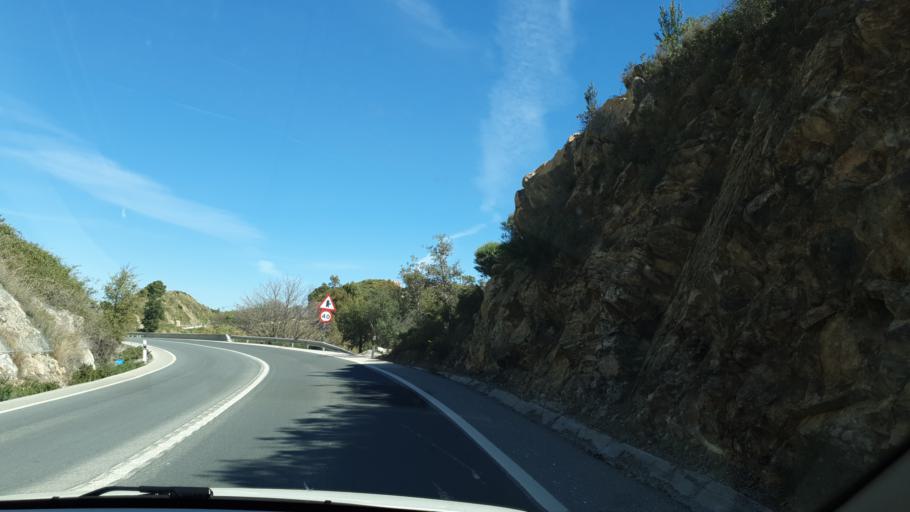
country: ES
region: Andalusia
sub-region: Provincia de Malaga
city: Ojen
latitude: 36.5811
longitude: -4.8528
